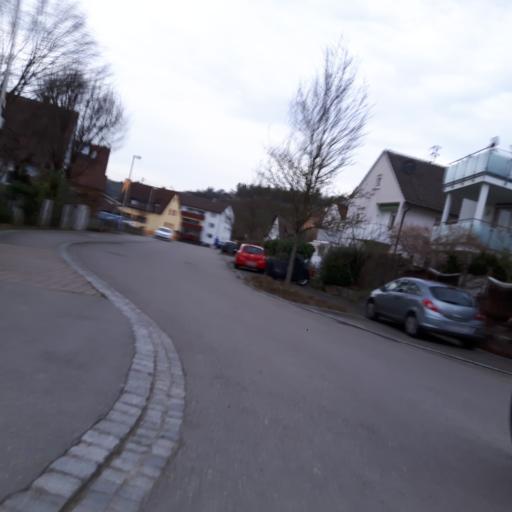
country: DE
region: Baden-Wuerttemberg
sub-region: Regierungsbezirk Stuttgart
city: Benningen am Neckar
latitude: 48.9465
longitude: 9.2472
